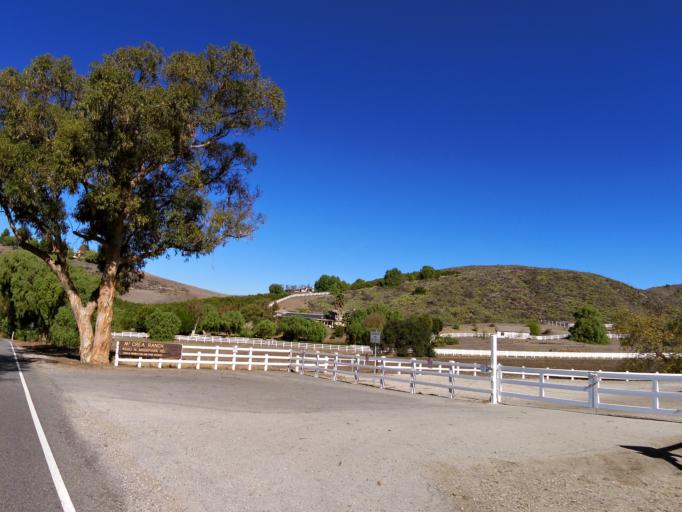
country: US
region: California
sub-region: Ventura County
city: Moorpark
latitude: 34.2443
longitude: -118.8634
